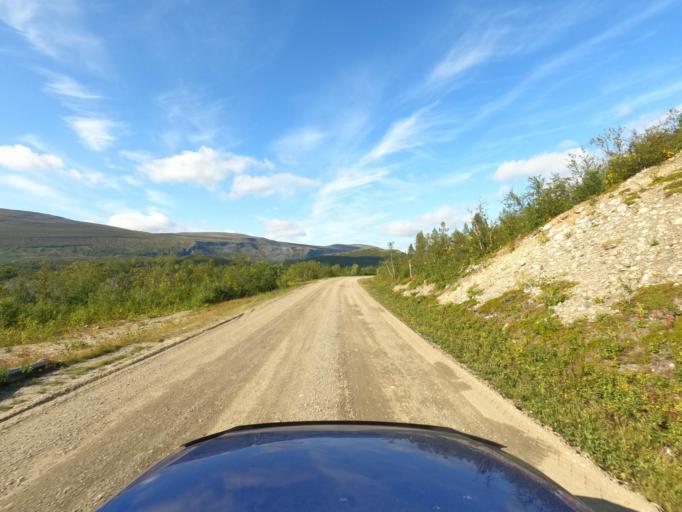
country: NO
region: Finnmark Fylke
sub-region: Porsanger
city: Lakselv
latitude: 69.8925
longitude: 24.9951
